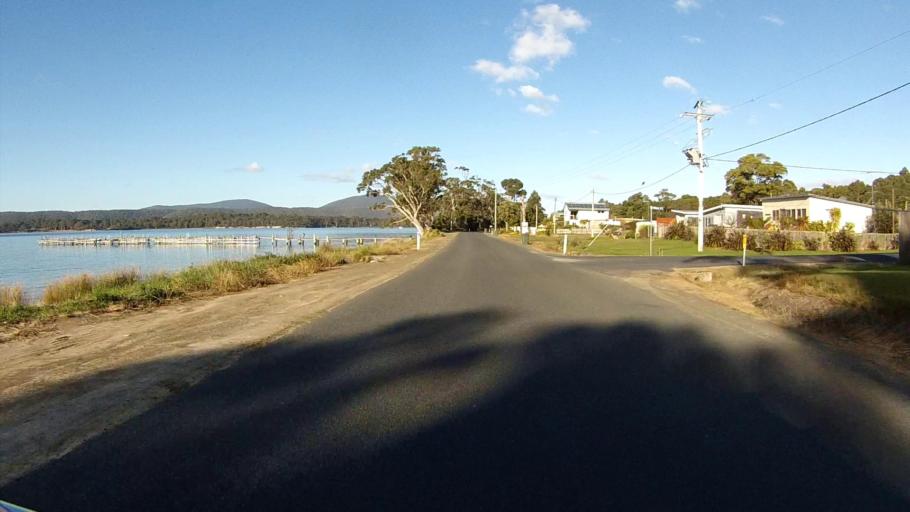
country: AU
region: Tasmania
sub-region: Clarence
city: Sandford
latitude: -43.1558
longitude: 147.8470
